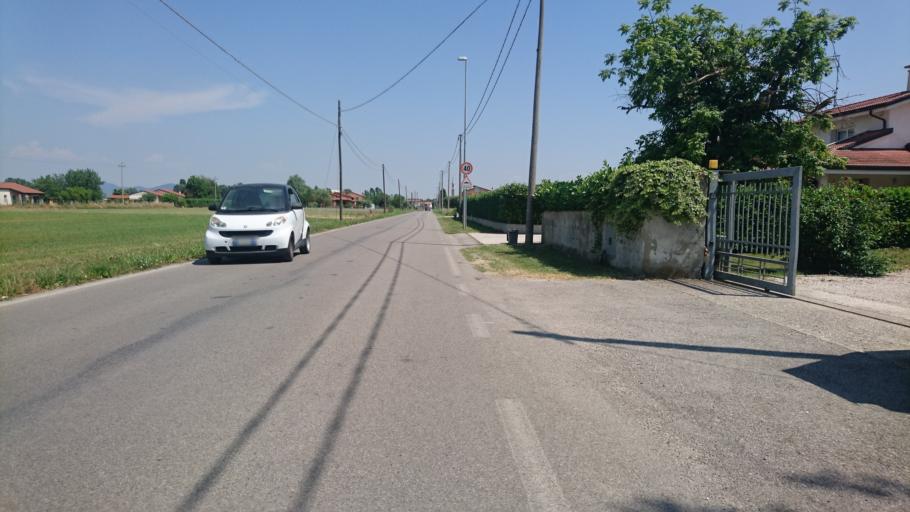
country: IT
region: Veneto
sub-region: Provincia di Padova
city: Solesino
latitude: 45.1669
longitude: 11.7373
